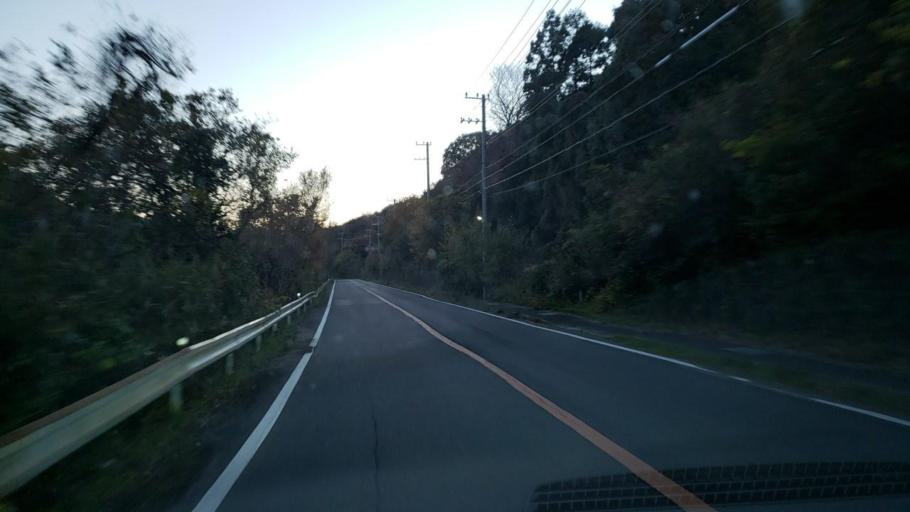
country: JP
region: Hyogo
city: Fukura
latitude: 34.2853
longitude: 134.7082
